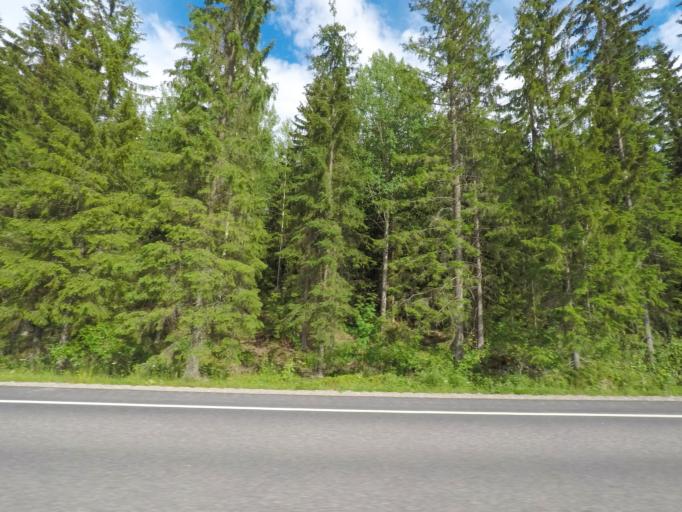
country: FI
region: Uusimaa
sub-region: Porvoo
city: Pukkila
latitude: 60.7932
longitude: 25.4673
